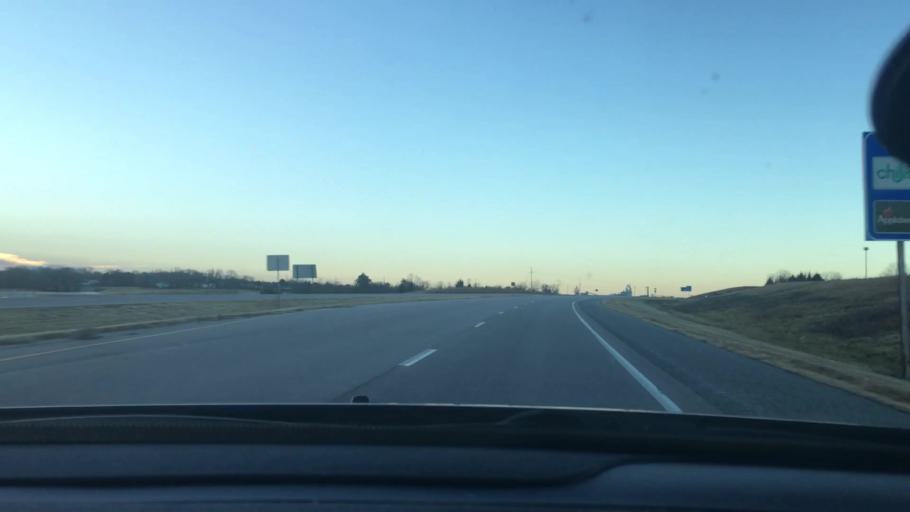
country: US
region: Oklahoma
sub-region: Pontotoc County
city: Ada
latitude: 34.8047
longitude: -96.6952
